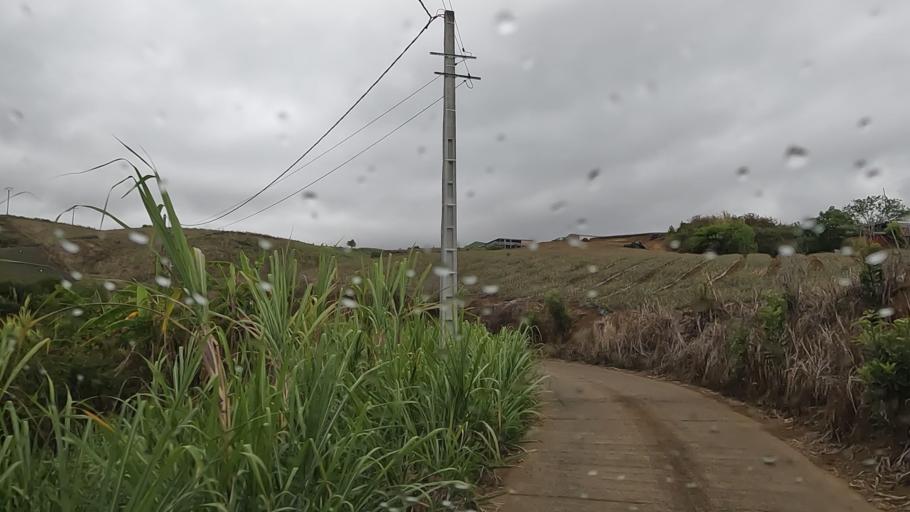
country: RE
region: Reunion
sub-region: Reunion
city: Le Tampon
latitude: -21.2903
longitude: 55.5441
